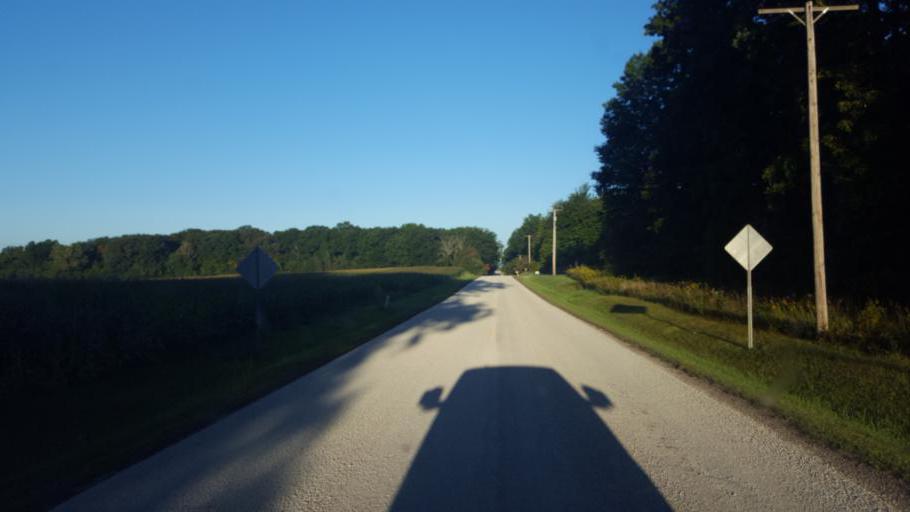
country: US
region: Ohio
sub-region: Wayne County
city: West Salem
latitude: 40.9923
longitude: -82.2259
